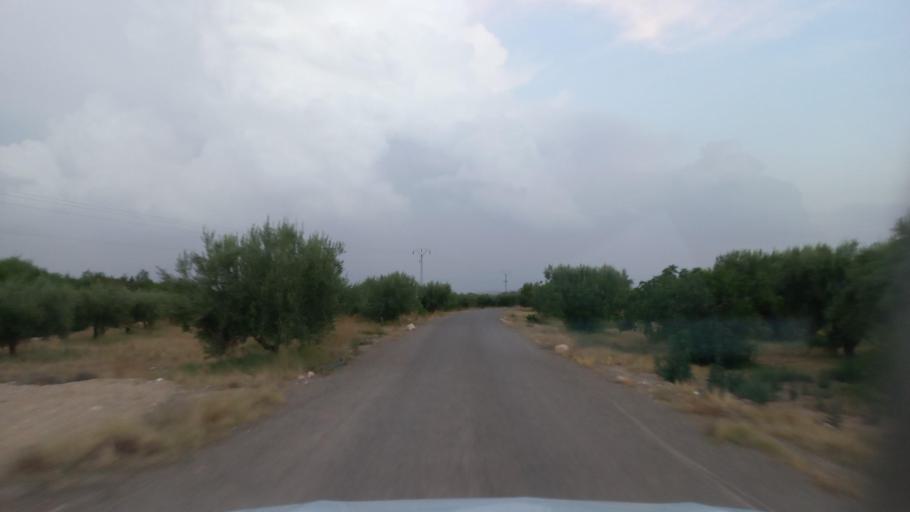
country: TN
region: Al Qasrayn
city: Kasserine
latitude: 35.2730
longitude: 9.0367
